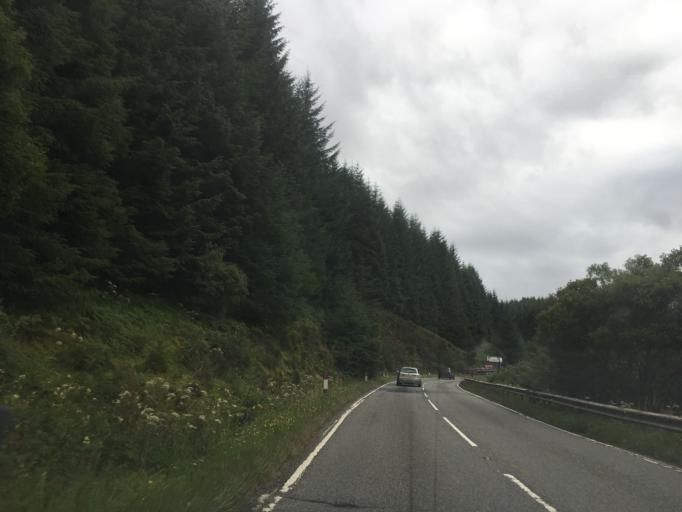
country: GB
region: Scotland
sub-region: Argyll and Bute
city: Oban
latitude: 56.2866
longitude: -5.4757
